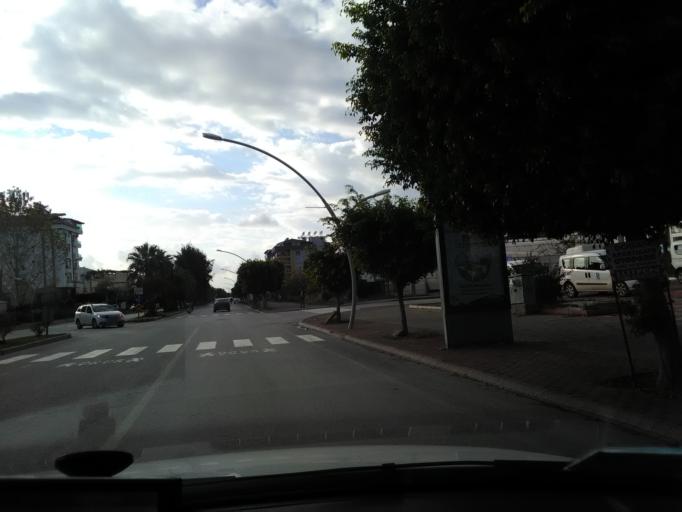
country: TR
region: Antalya
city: Gazipasa
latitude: 36.2676
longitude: 32.3086
